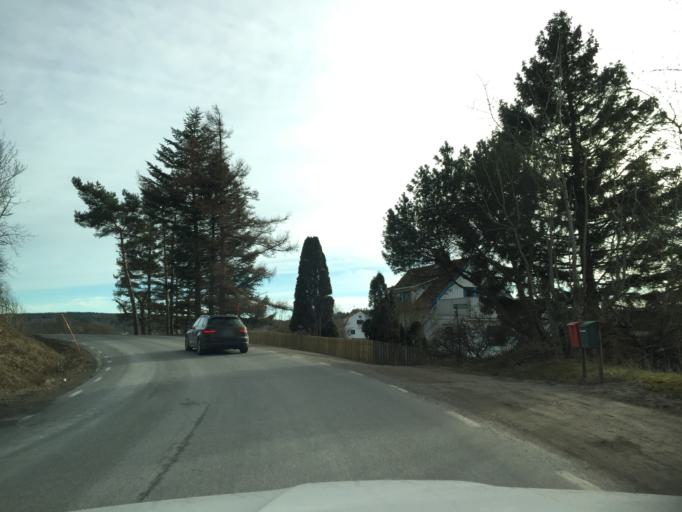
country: SE
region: Vaestra Goetaland
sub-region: Tjorns Kommun
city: Skaerhamn
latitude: 58.0277
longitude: 11.6041
